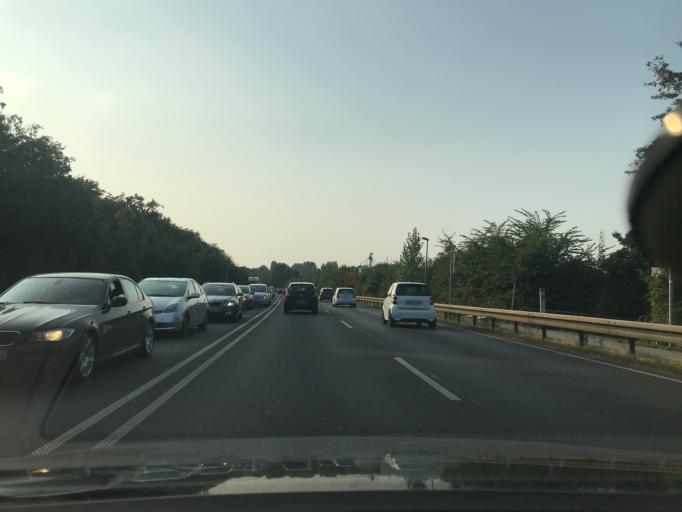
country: DE
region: North Rhine-Westphalia
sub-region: Regierungsbezirk Dusseldorf
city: Erkrath
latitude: 51.1933
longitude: 6.9140
